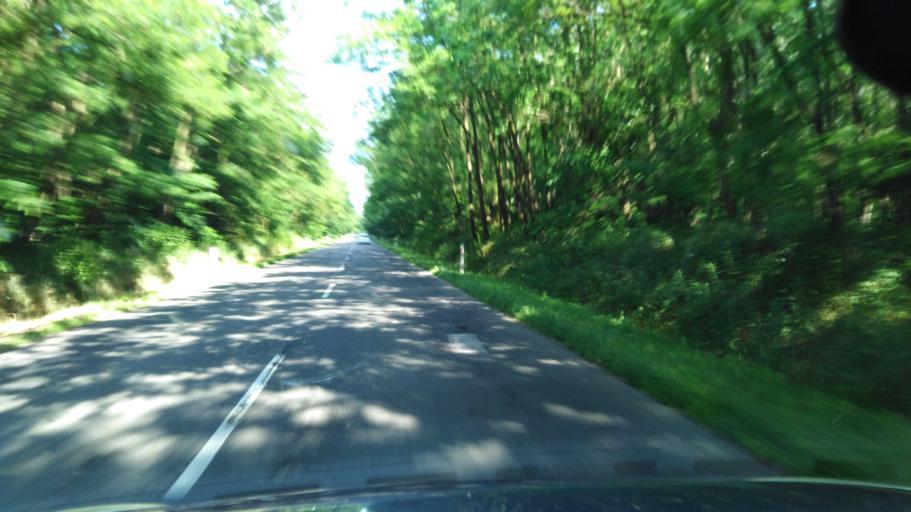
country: HU
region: Szabolcs-Szatmar-Bereg
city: Nyirvasvari
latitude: 47.8078
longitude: 22.2381
